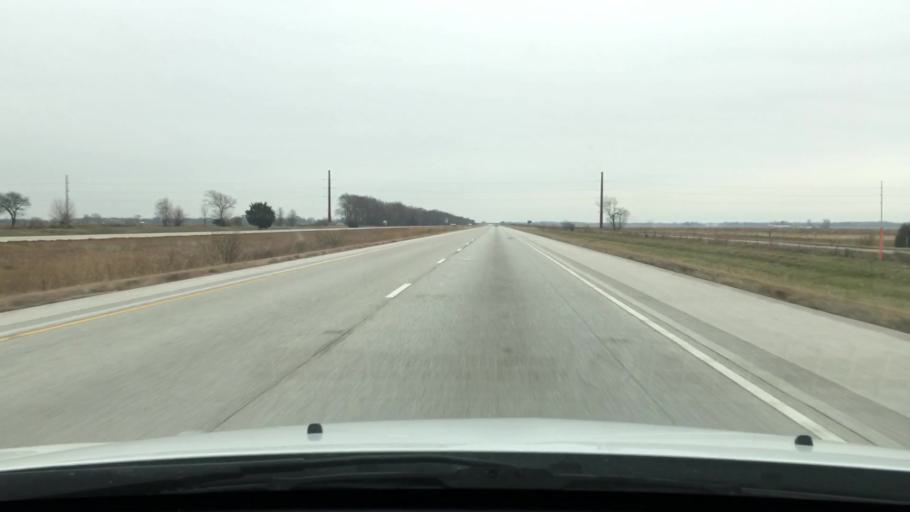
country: US
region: Illinois
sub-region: Scott County
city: Winchester
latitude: 39.6801
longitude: -90.3771
